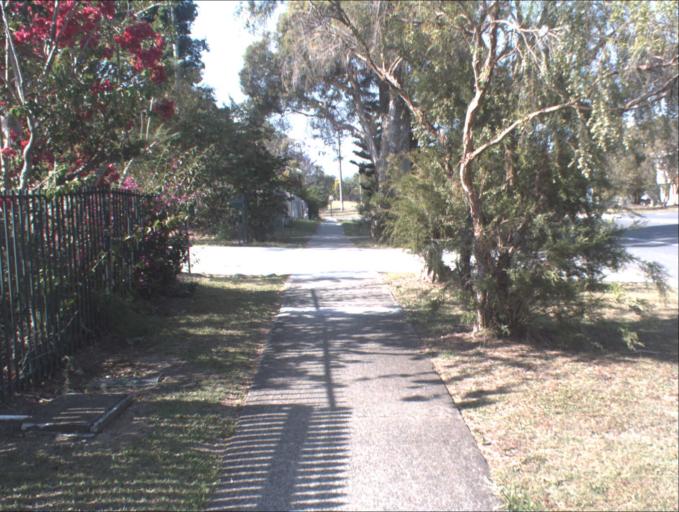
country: AU
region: Queensland
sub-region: Logan
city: Beenleigh
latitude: -27.6922
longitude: 153.1791
